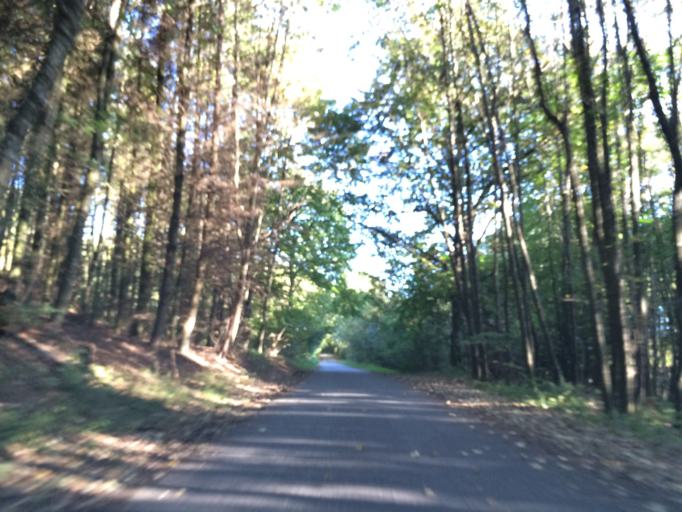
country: DK
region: Central Jutland
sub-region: Randers Kommune
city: Langa
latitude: 56.3554
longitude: 9.9293
